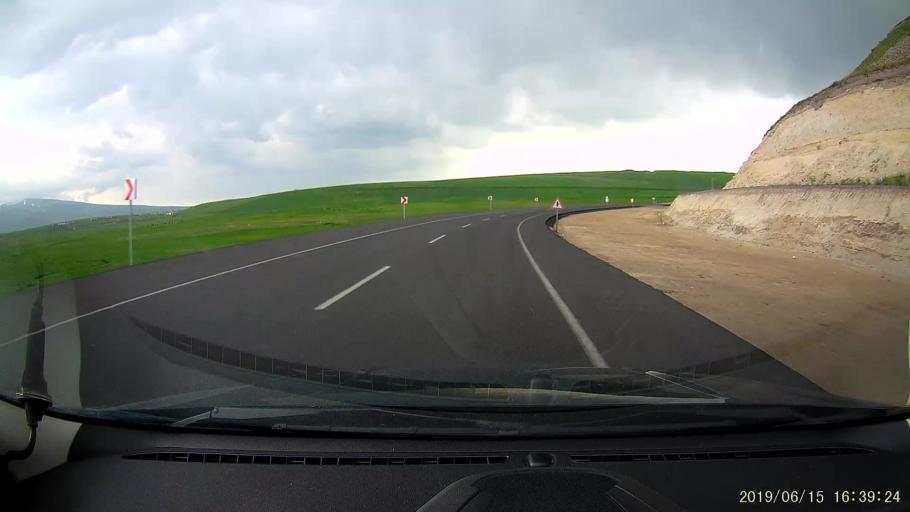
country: TR
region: Ardahan
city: Haskoy
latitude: 40.9832
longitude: 42.8972
